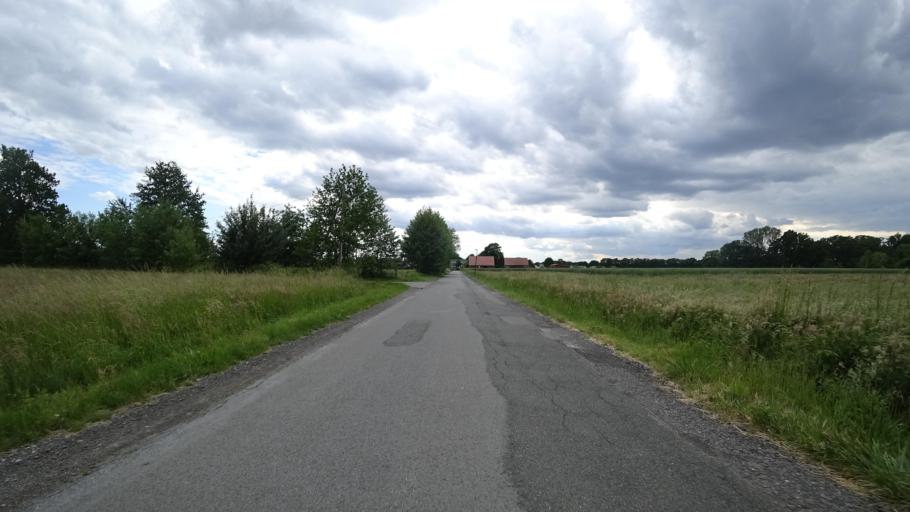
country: DE
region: North Rhine-Westphalia
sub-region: Regierungsbezirk Detmold
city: Guetersloh
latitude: 51.8974
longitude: 8.4427
